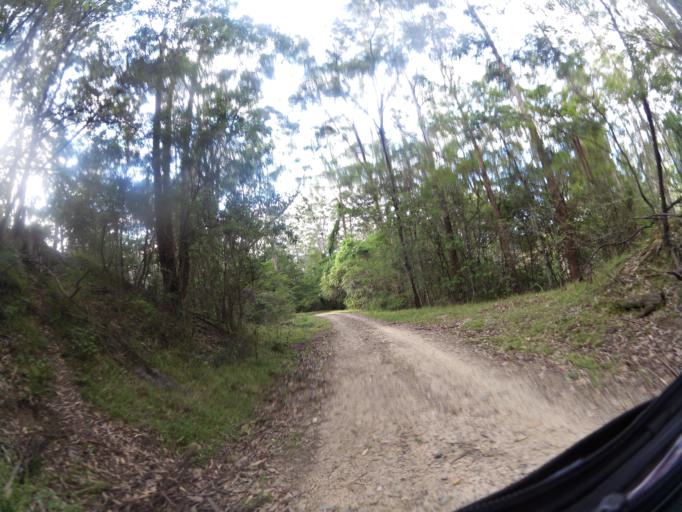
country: AU
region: Victoria
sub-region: East Gippsland
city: Lakes Entrance
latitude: -37.7285
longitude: 148.4250
